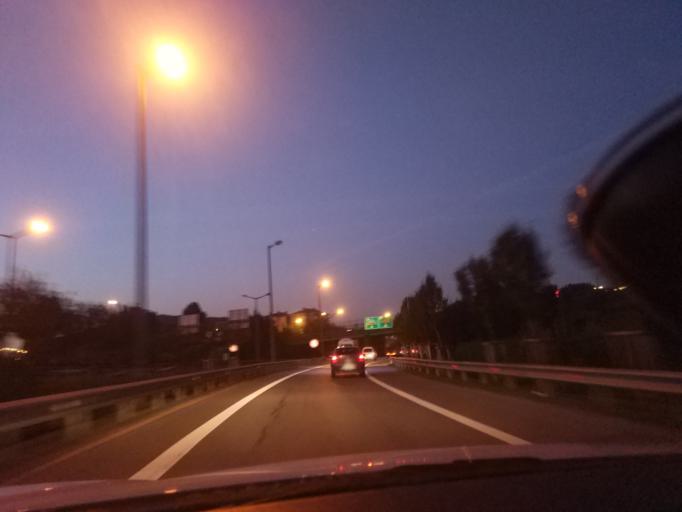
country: TR
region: Istanbul
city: Sultanbeyli
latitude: 40.9353
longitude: 29.3312
